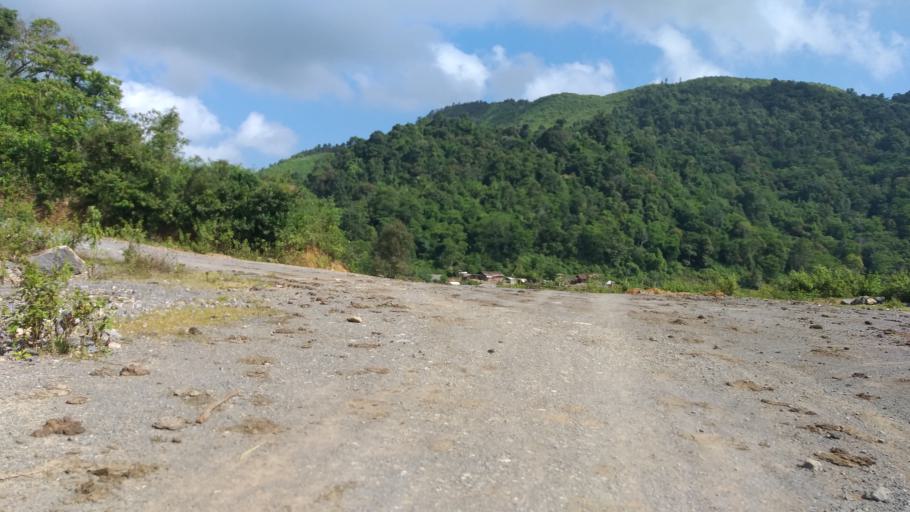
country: LA
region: Phongsali
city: Khoa
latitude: 21.2215
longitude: 102.5978
